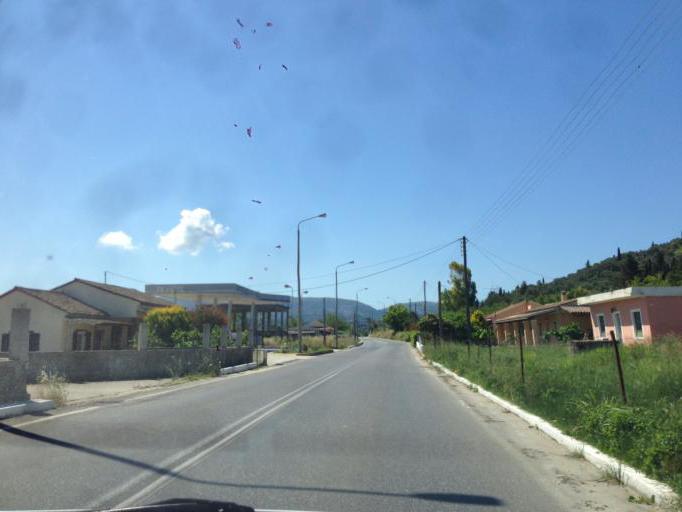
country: GR
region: Ionian Islands
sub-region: Nomos Kerkyras
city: Agios Georgis
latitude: 39.7665
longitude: 19.7169
